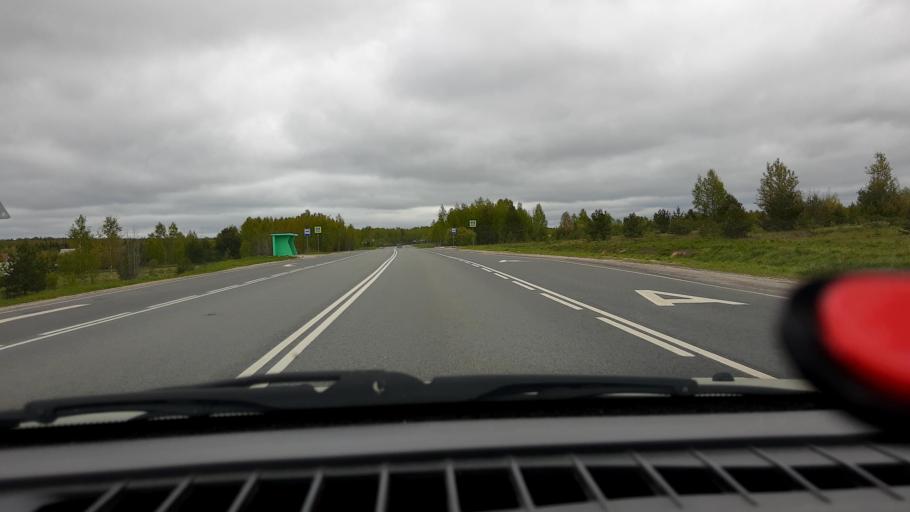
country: RU
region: Nizjnij Novgorod
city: Semenov
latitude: 56.7291
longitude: 44.2972
